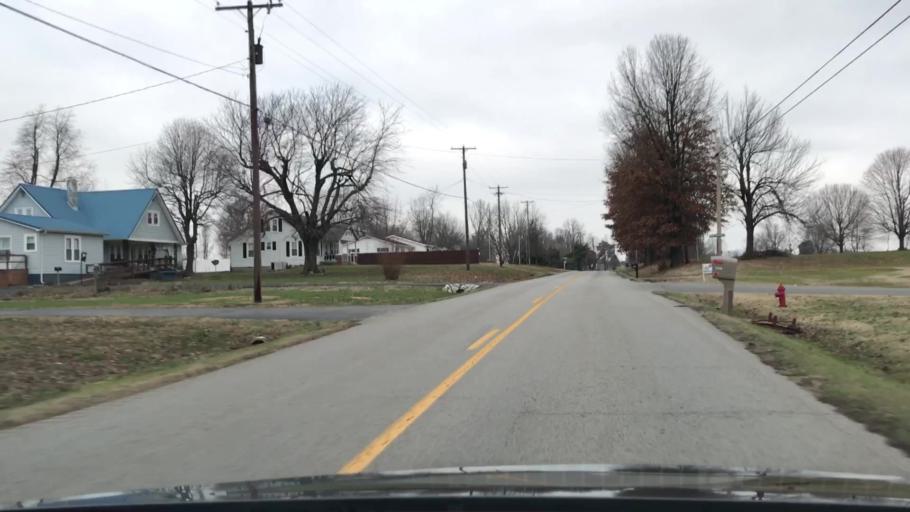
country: US
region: Kentucky
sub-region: Muhlenberg County
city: Morehead
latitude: 37.3894
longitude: -87.2537
